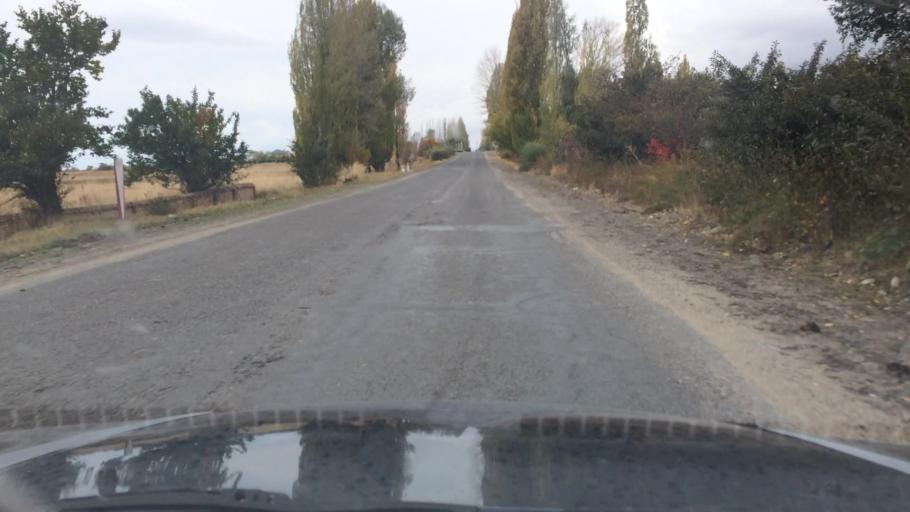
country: KG
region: Ysyk-Koel
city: Pokrovka
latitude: 42.7366
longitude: 77.9534
